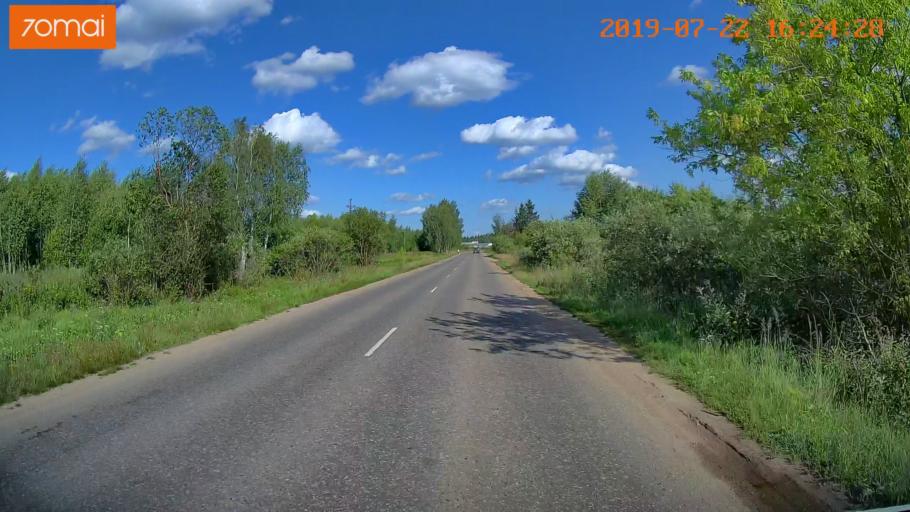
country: RU
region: Ivanovo
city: Novo-Talitsy
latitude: 57.0581
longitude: 40.9138
